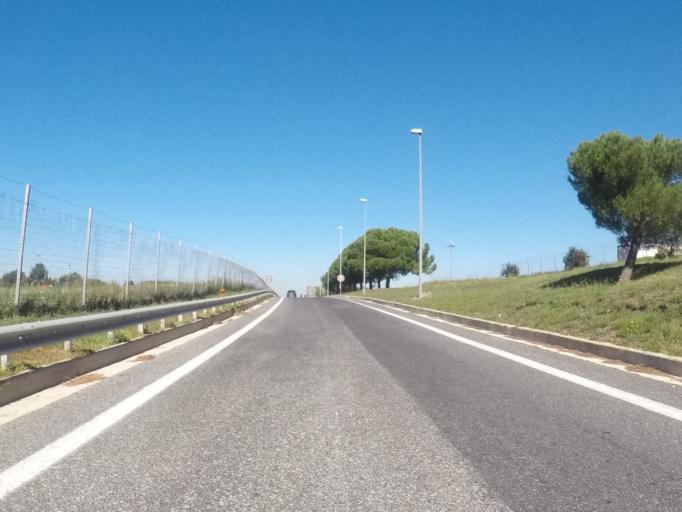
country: IT
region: Latium
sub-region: Citta metropolitana di Roma Capitale
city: Valle Martella
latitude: 41.8887
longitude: 12.7607
